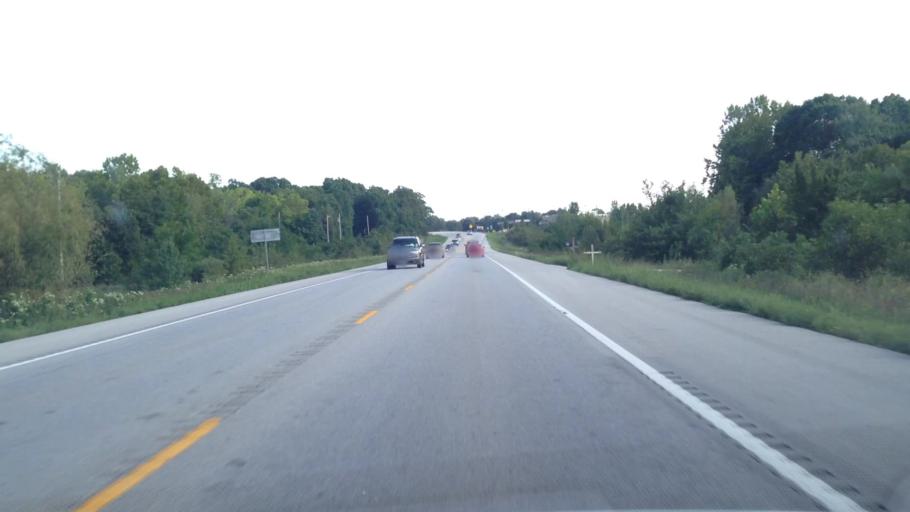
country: US
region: Missouri
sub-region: Jasper County
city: Carl Junction
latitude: 37.1495
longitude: -94.5246
